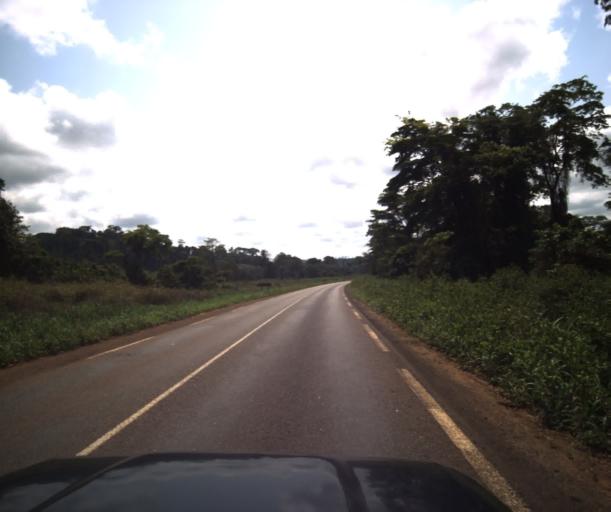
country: CM
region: Centre
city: Eseka
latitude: 3.8896
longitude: 10.7958
